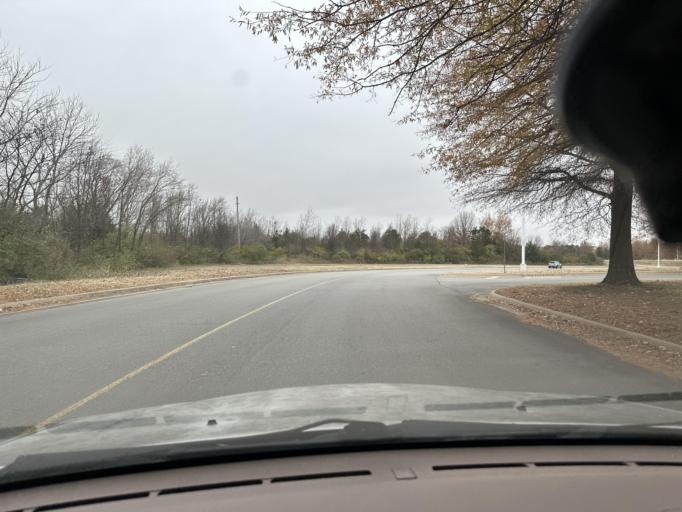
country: US
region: Arkansas
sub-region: Washington County
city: Johnson
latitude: 36.1259
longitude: -94.1513
